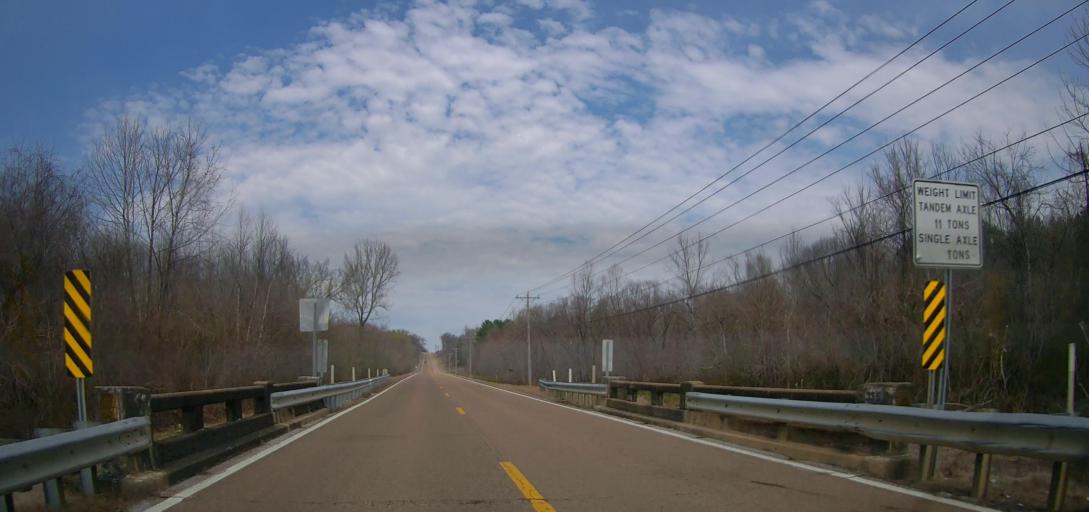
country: US
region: Mississippi
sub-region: Marshall County
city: Holly Springs
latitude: 34.7291
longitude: -89.4190
